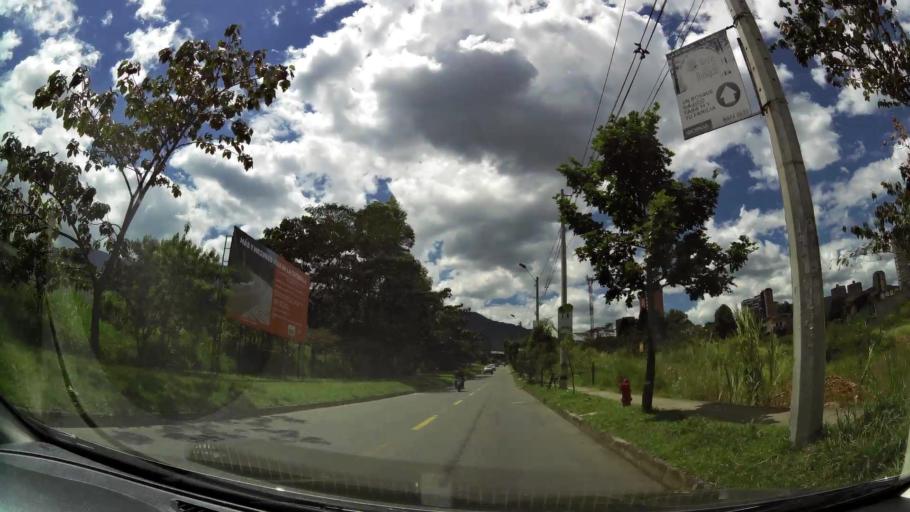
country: CO
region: Antioquia
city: La Estrella
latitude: 6.1593
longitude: -75.6309
